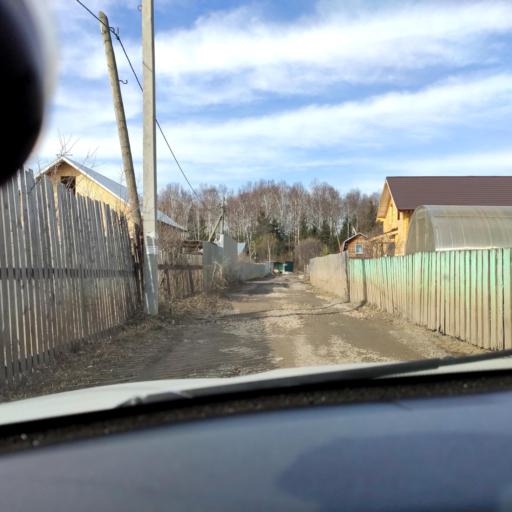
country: RU
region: Perm
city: Overyata
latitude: 58.0588
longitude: 55.9865
